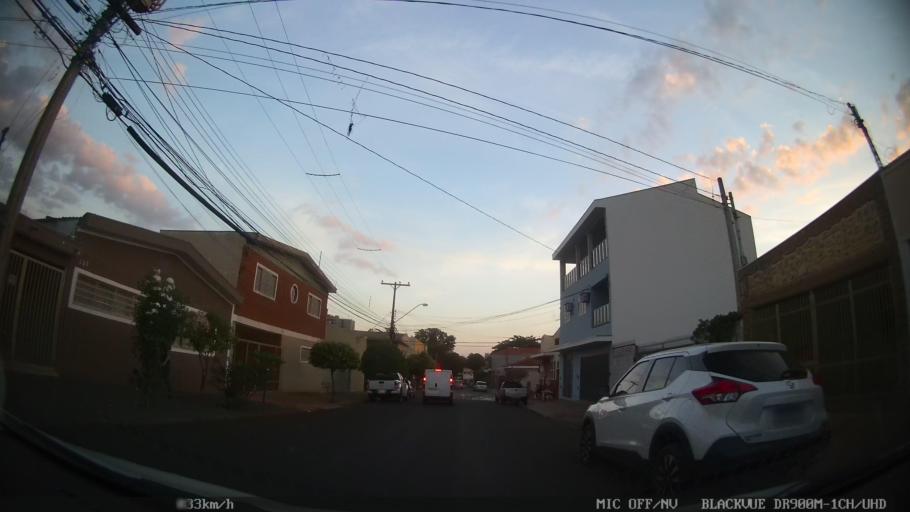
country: BR
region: Sao Paulo
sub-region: Ribeirao Preto
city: Ribeirao Preto
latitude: -21.1557
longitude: -47.8311
